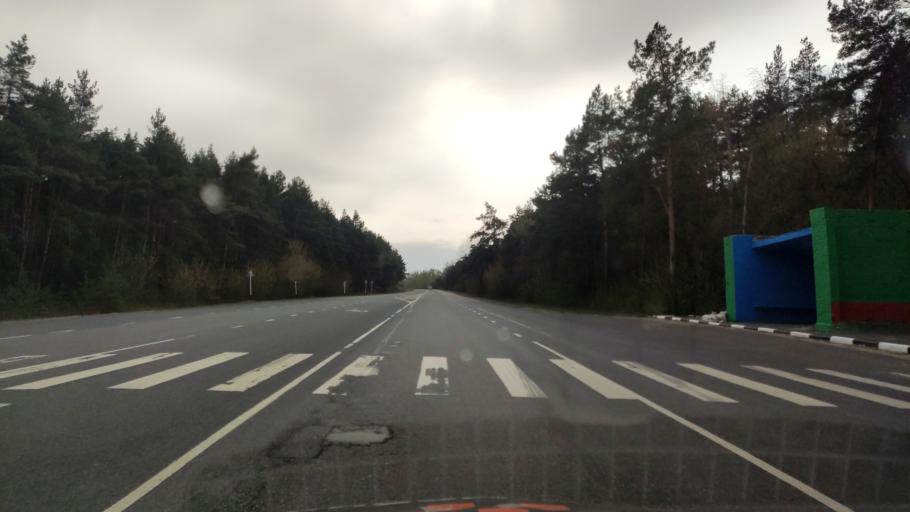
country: RU
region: Kursk
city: Gorshechnoye
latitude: 51.4676
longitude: 37.9328
